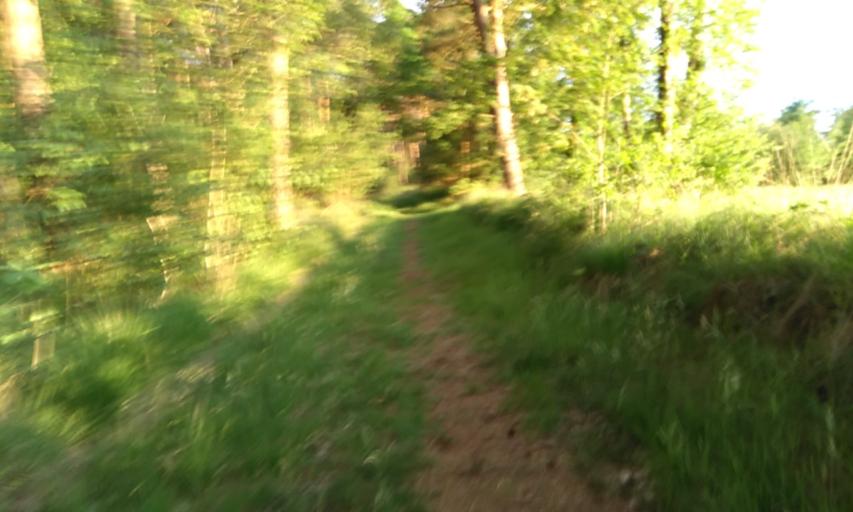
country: DE
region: Lower Saxony
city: Agathenburg
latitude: 53.5280
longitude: 9.4984
